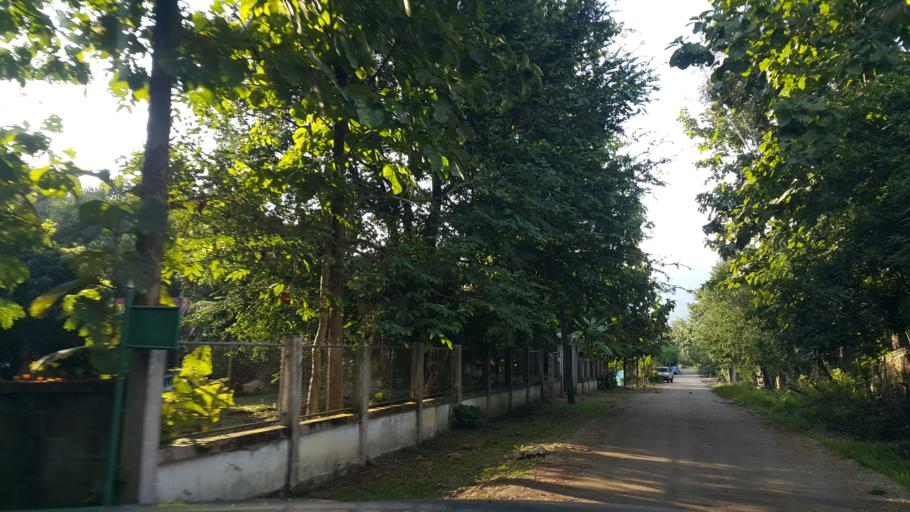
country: TH
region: Chiang Mai
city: Mae On
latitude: 18.7394
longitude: 99.2380
